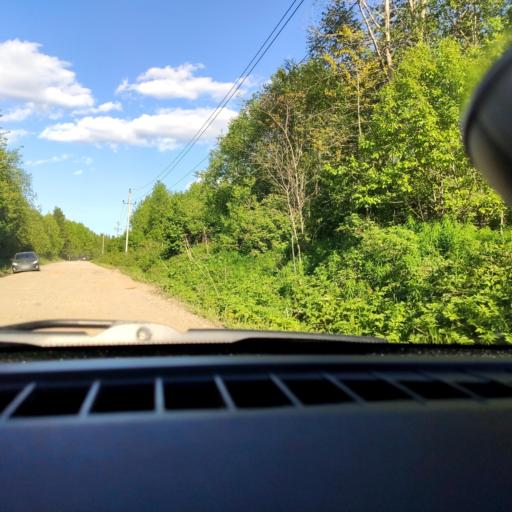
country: RU
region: Perm
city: Polazna
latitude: 58.2922
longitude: 56.1454
